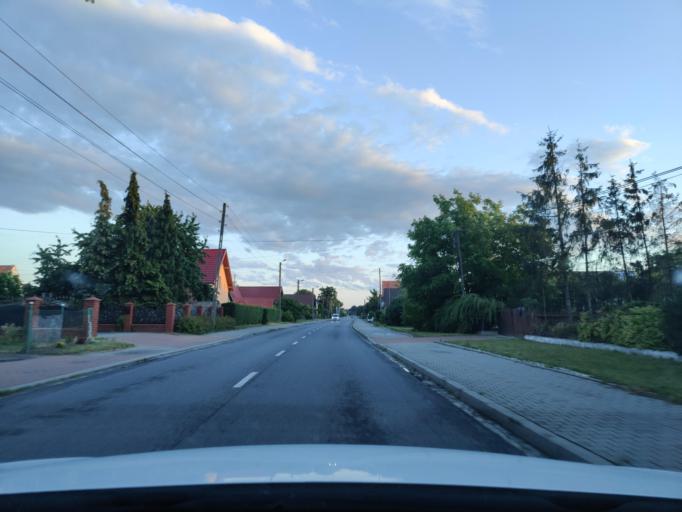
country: PL
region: Opole Voivodeship
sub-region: Powiat nyski
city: Chroscina
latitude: 50.6542
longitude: 17.3876
